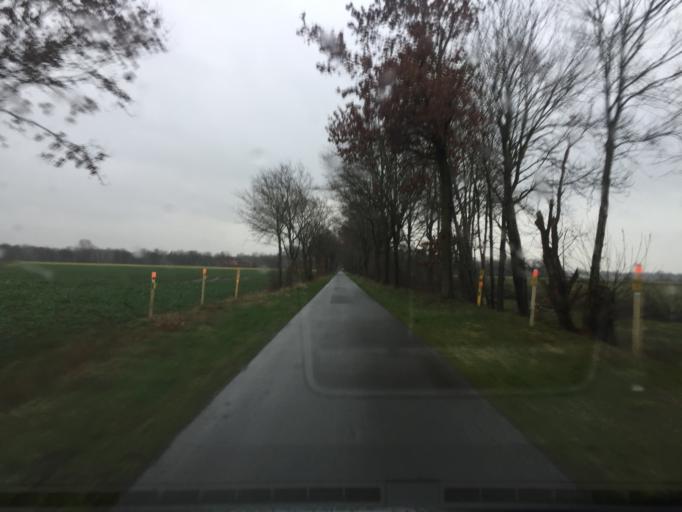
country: DE
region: Lower Saxony
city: Borstel
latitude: 52.6170
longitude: 8.9117
